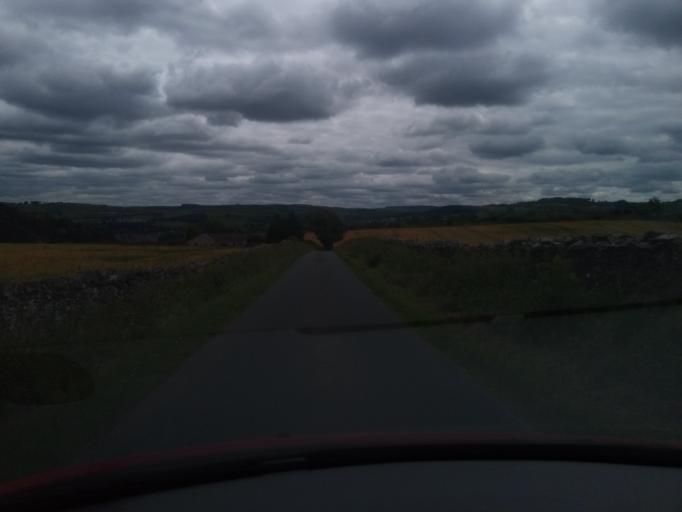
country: GB
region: Scotland
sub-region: The Scottish Borders
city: Hawick
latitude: 55.4253
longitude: -2.8152
